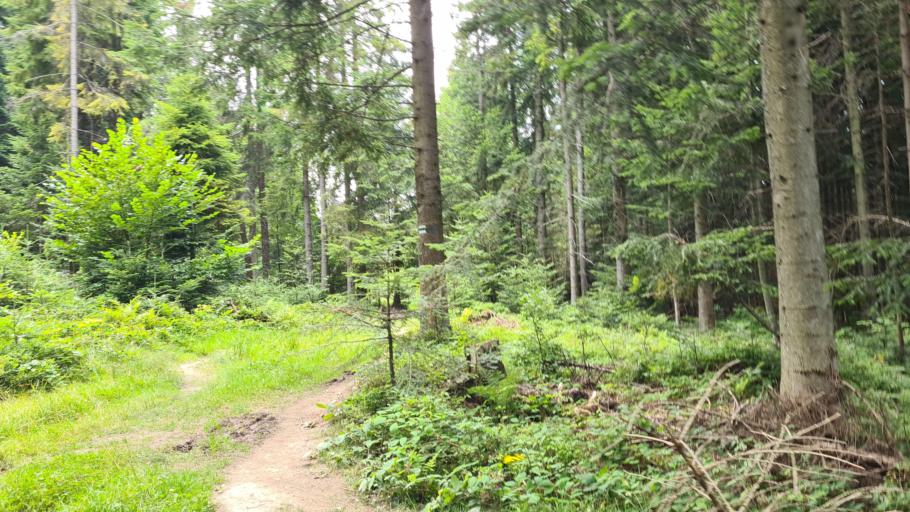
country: PL
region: Lesser Poland Voivodeship
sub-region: Powiat nowosadecki
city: Rytro
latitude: 49.4169
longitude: 20.6222
